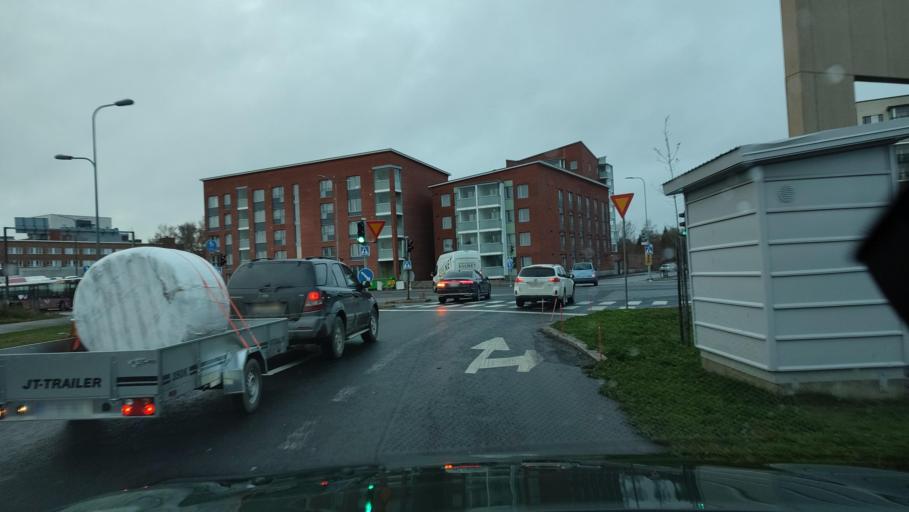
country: FI
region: Ostrobothnia
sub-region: Vaasa
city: Vaasa
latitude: 63.0993
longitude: 21.6335
